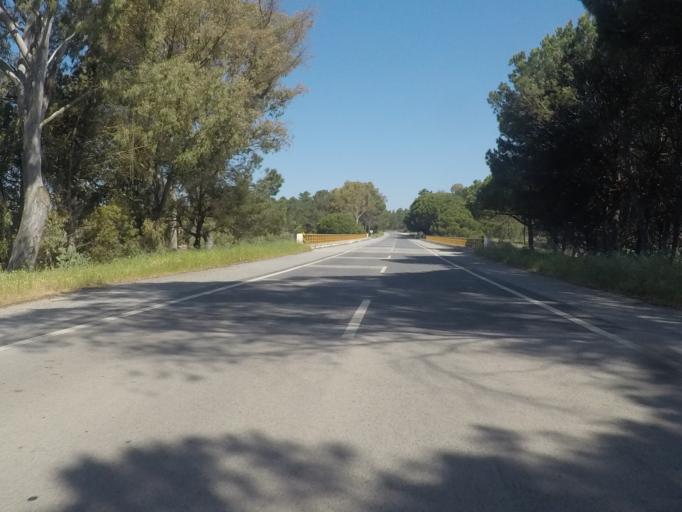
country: PT
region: Setubal
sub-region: Grandola
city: Grandola
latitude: 38.3129
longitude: -8.7445
